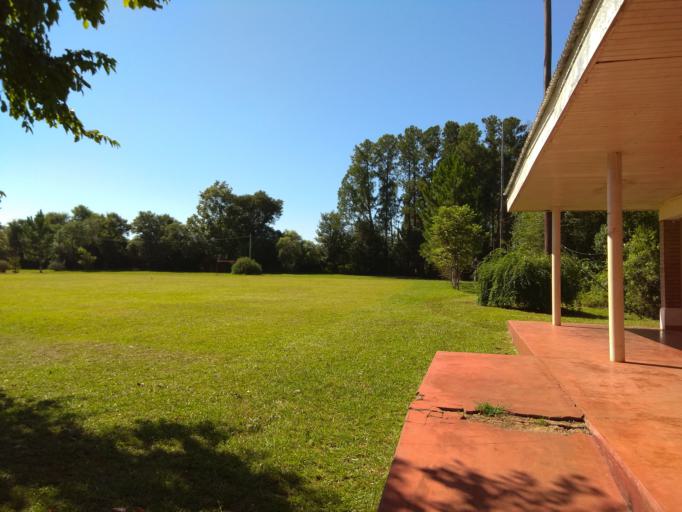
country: AR
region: Misiones
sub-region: Departamento de Apostoles
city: Apostoles
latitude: -27.9851
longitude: -55.7851
